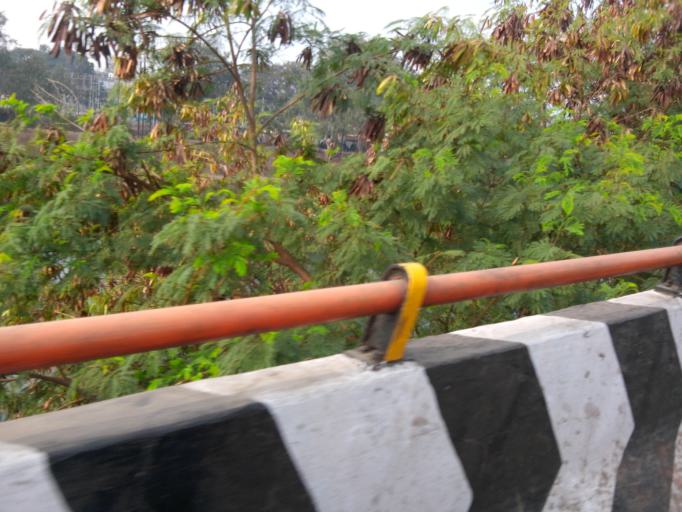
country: IN
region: Andhra Pradesh
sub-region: Krishna
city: Vijayawada
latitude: 16.5112
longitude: 80.6161
